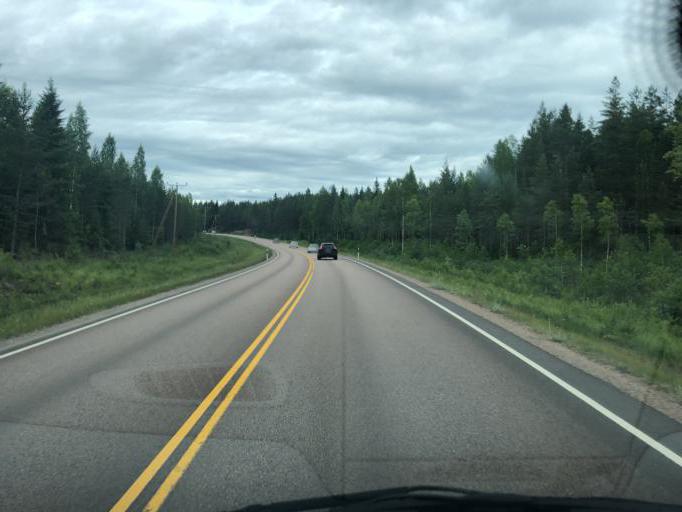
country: FI
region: Southern Savonia
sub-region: Mikkeli
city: Ristiina
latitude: 61.1641
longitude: 27.1467
